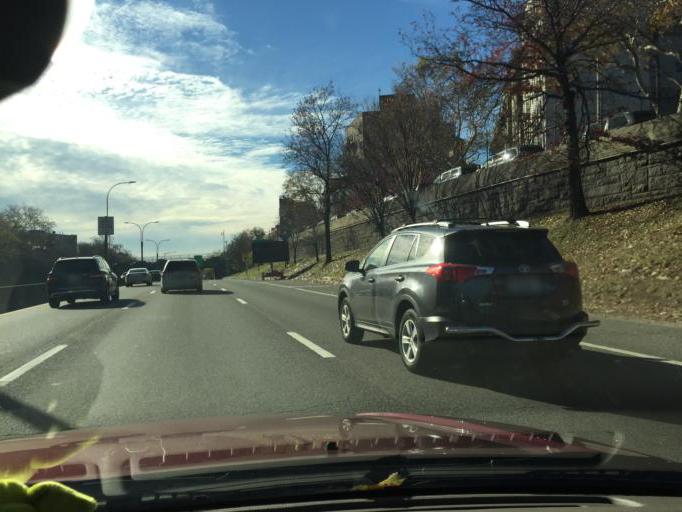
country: US
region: New York
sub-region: Queens County
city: Long Island City
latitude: 40.7068
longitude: -73.9583
